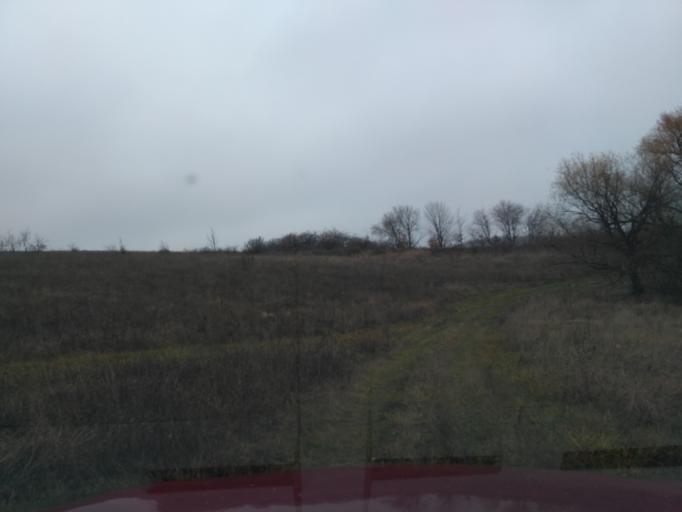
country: SK
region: Kosicky
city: Kosice
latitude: 48.7818
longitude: 21.2203
